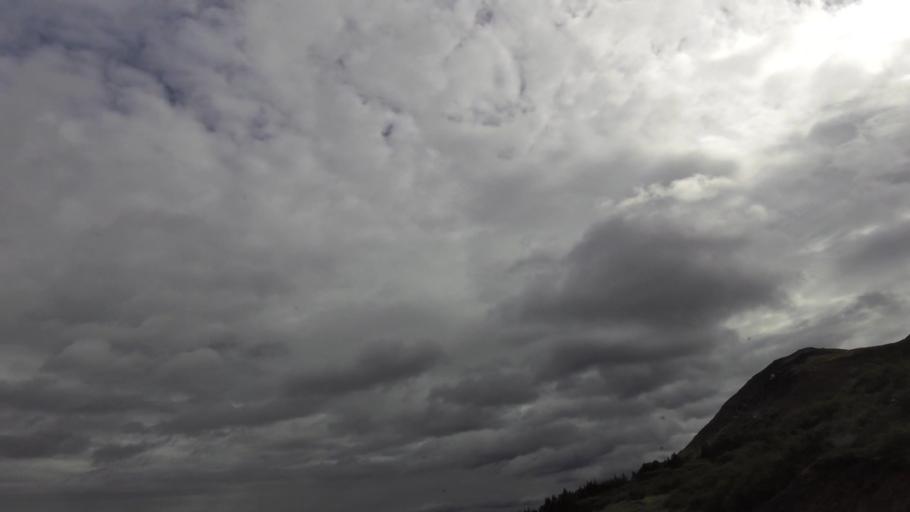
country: IS
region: West
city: Stykkisholmur
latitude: 65.5204
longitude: -22.1160
